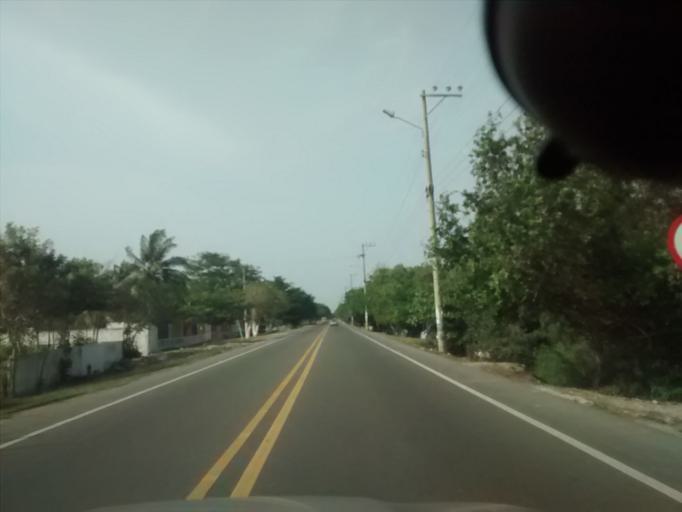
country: CO
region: Bolivar
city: Cartagena
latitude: 10.4704
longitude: -75.4967
